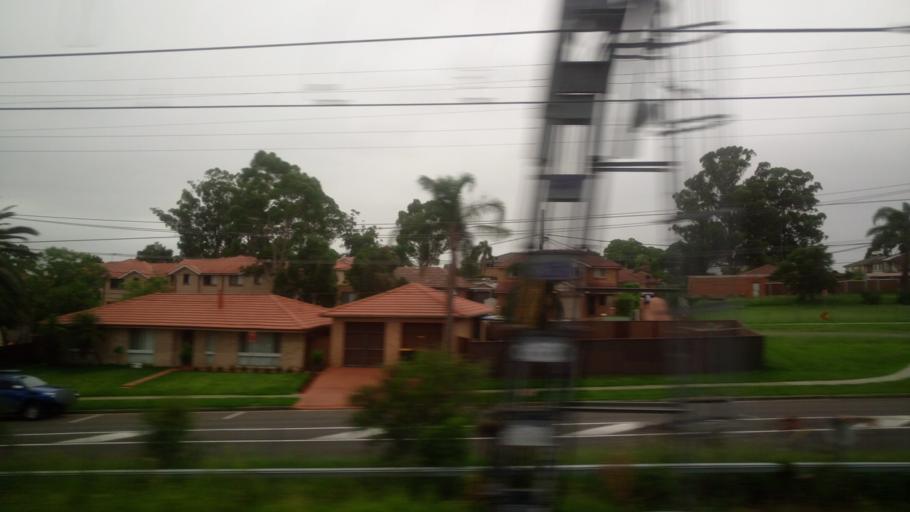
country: AU
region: New South Wales
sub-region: Blacktown
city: Doonside
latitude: -33.7634
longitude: 150.8733
